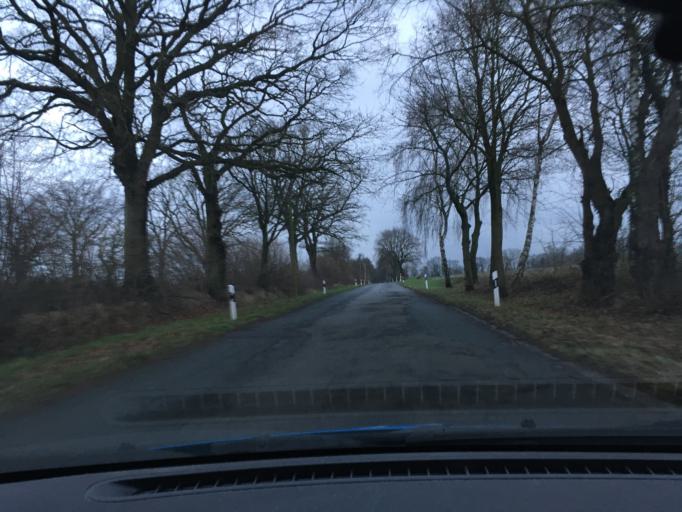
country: DE
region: Mecklenburg-Vorpommern
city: Nostorf
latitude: 53.3983
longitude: 10.6831
